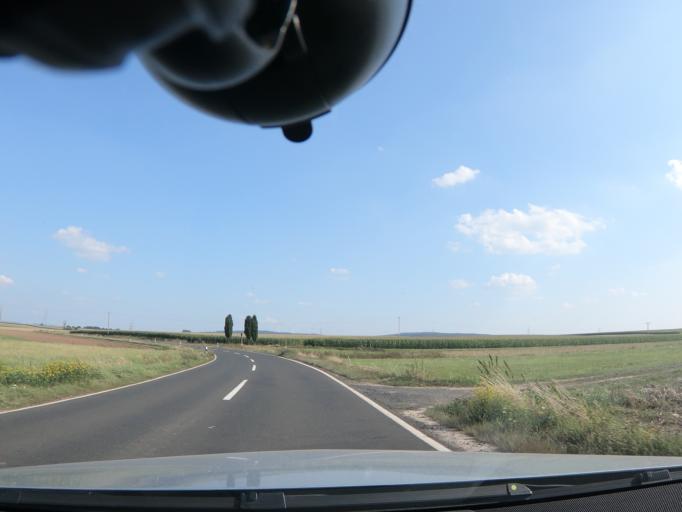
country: DE
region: Hesse
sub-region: Regierungsbezirk Giessen
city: Ebsdorfergrund
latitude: 50.7834
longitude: 8.8409
